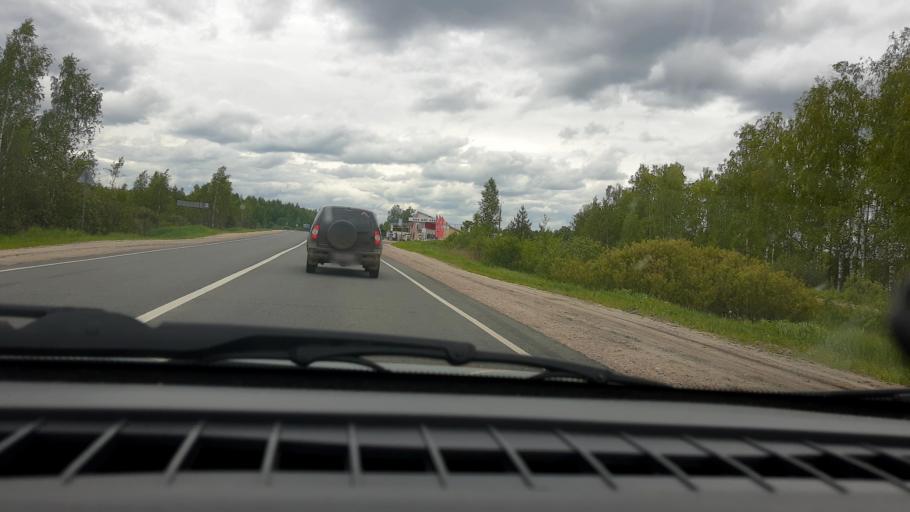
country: RU
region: Nizjnij Novgorod
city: Krasnyye Baki
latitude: 57.0884
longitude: 45.1478
